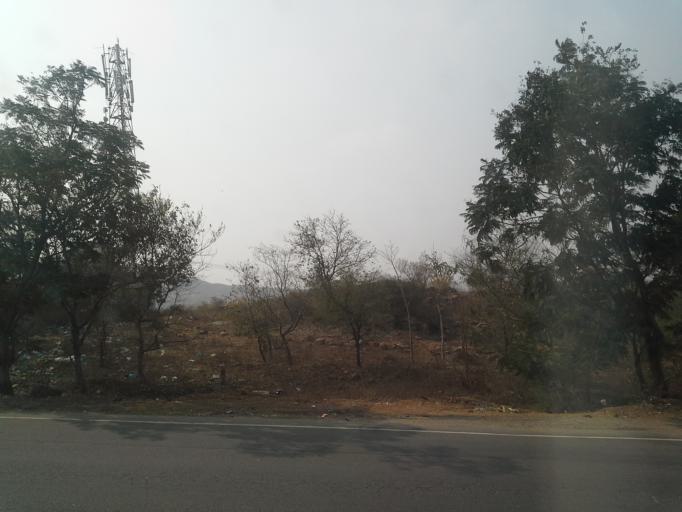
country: IN
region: Telangana
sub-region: Rangareddi
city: Lal Bahadur Nagar
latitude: 17.3163
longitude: 78.6694
